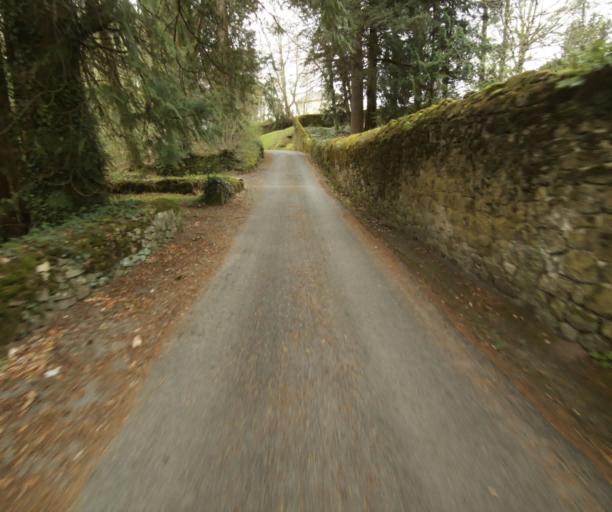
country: FR
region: Limousin
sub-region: Departement de la Correze
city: Argentat
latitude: 45.1948
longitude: 1.9718
